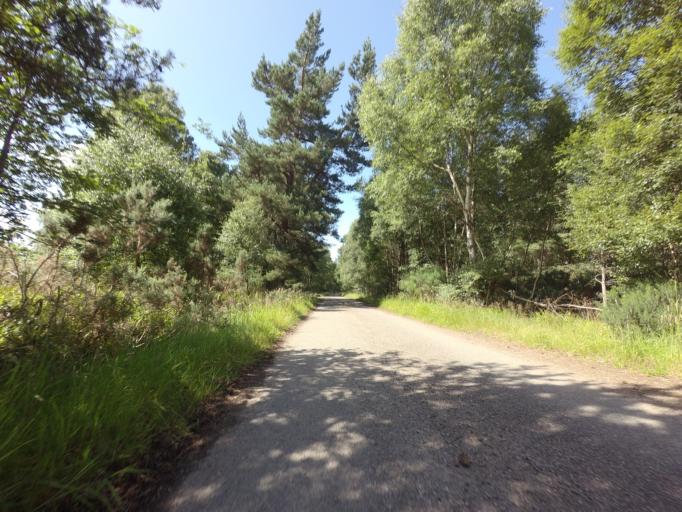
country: GB
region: Scotland
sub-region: Highland
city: Nairn
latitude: 57.5026
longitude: -3.9220
